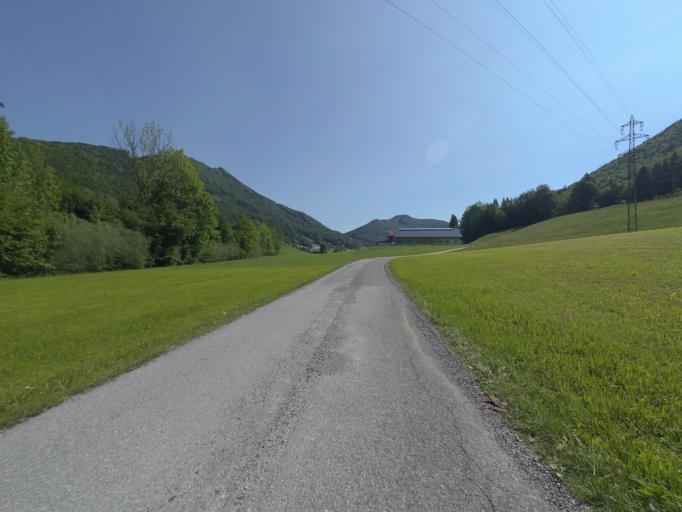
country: AT
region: Salzburg
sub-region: Politischer Bezirk Salzburg-Umgebung
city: Koppl
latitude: 47.7721
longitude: 13.1324
